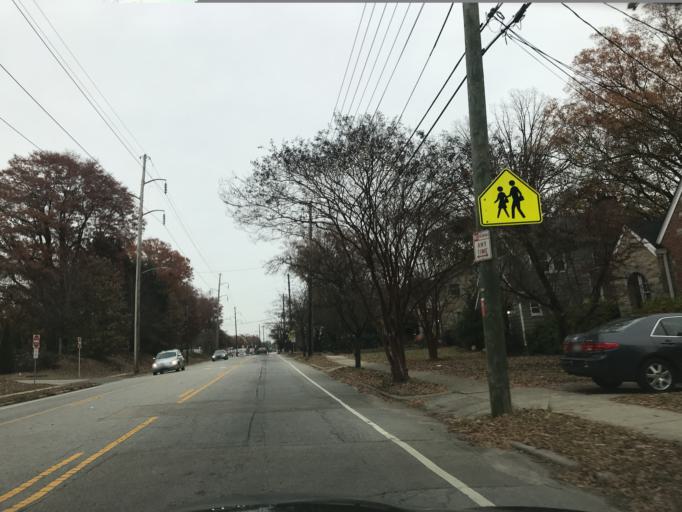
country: US
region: North Carolina
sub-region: Wake County
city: West Raleigh
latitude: 35.7886
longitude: -78.6534
